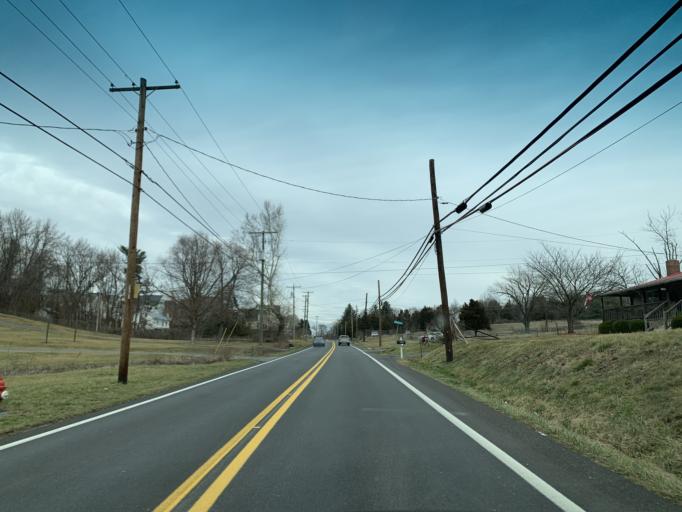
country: US
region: Maryland
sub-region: Washington County
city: Williamsport
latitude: 39.5718
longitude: -77.8809
